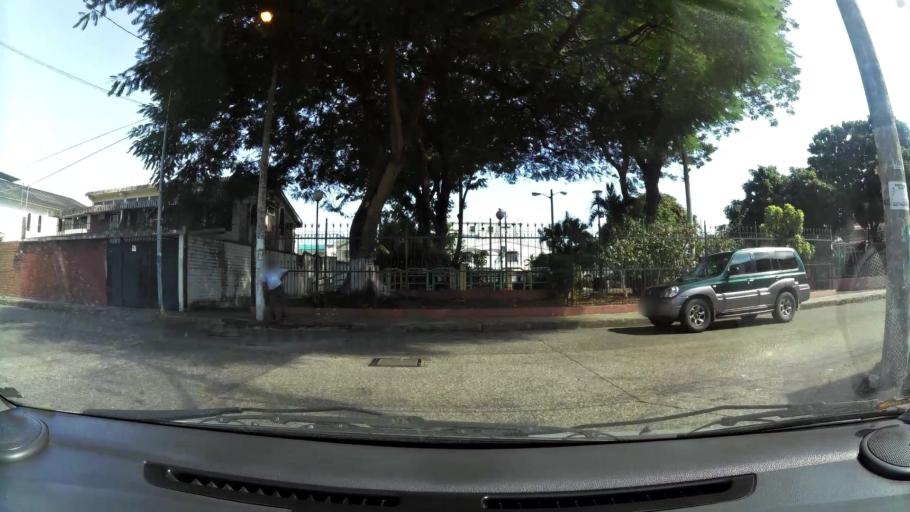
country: EC
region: Guayas
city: Guayaquil
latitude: -2.2254
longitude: -79.8950
